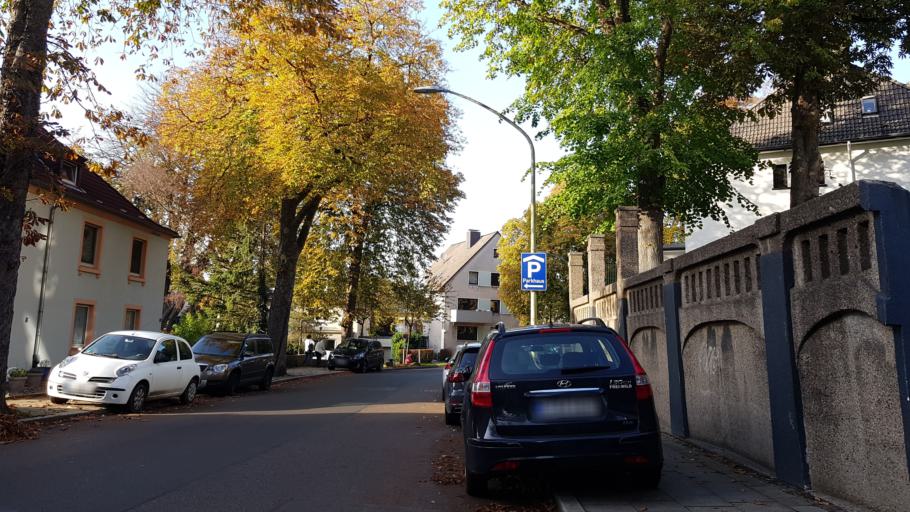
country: DE
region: North Rhine-Westphalia
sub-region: Regierungsbezirk Dusseldorf
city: Velbert
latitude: 51.3927
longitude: 7.0882
